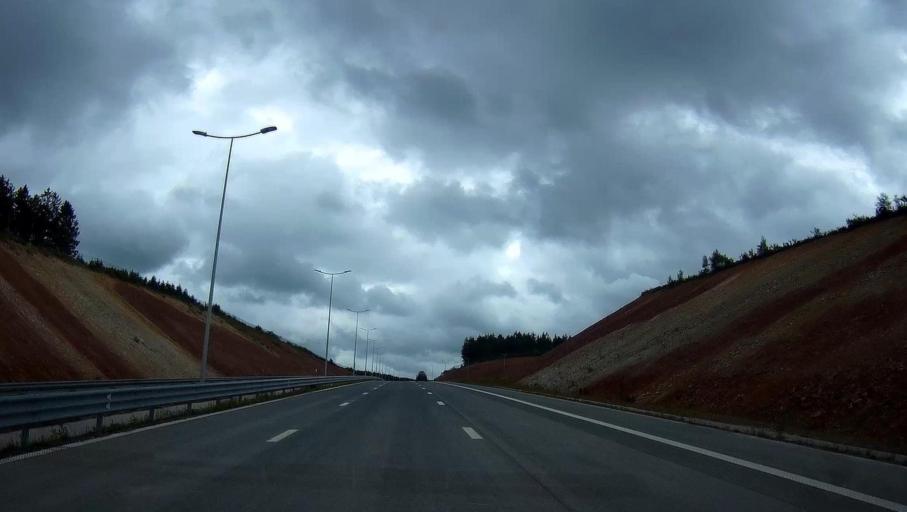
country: BE
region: Wallonia
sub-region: Province de Namur
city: Couvin
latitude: 50.0277
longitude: 4.5142
